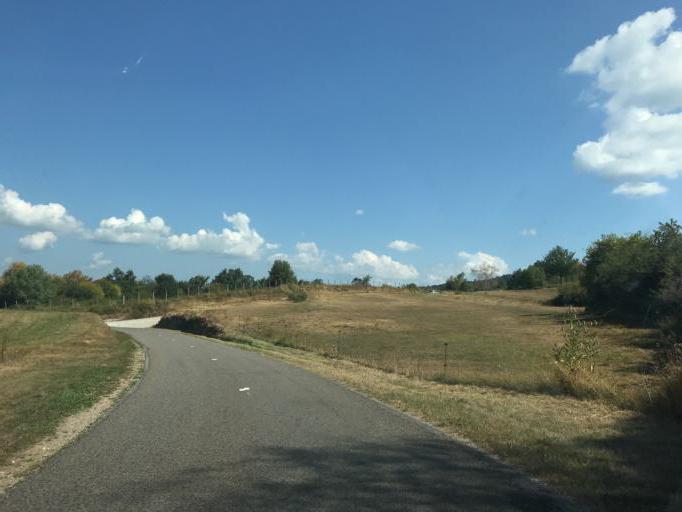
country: FR
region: Franche-Comte
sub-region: Departement du Jura
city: Moirans-en-Montagne
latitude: 46.4638
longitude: 5.7258
